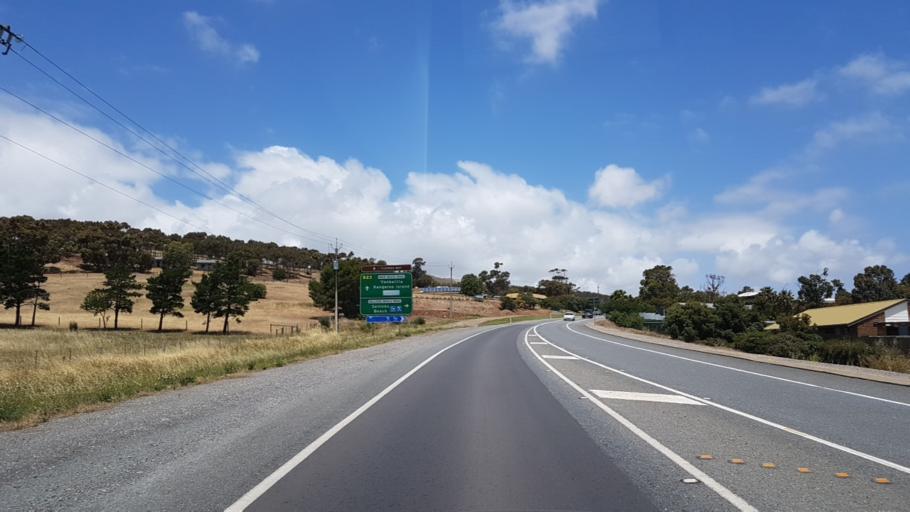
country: AU
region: South Australia
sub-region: Onkaparinga
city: Aldinga
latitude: -35.3260
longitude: 138.4746
